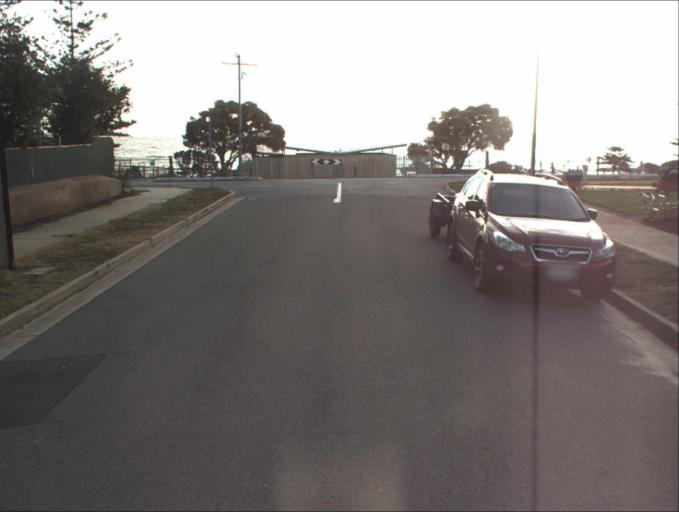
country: AU
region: South Australia
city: Port Adelaide
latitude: -34.8449
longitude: 138.4787
